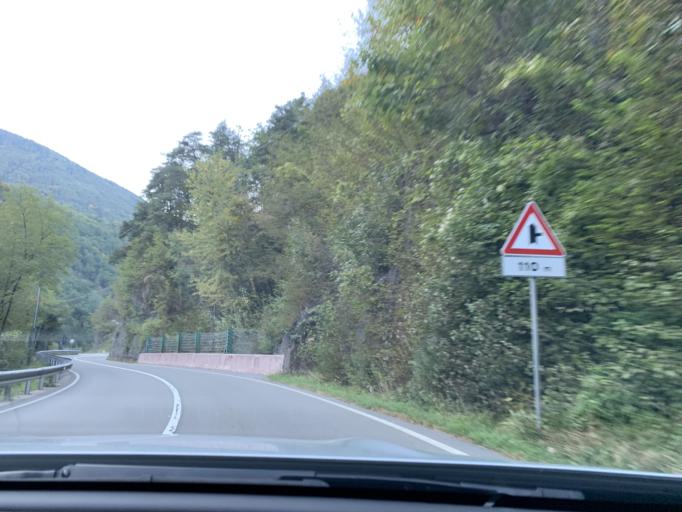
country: IT
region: Trentino-Alto Adige
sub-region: Bolzano
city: Cornedo All'Isarco
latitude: 46.4642
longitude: 11.4136
